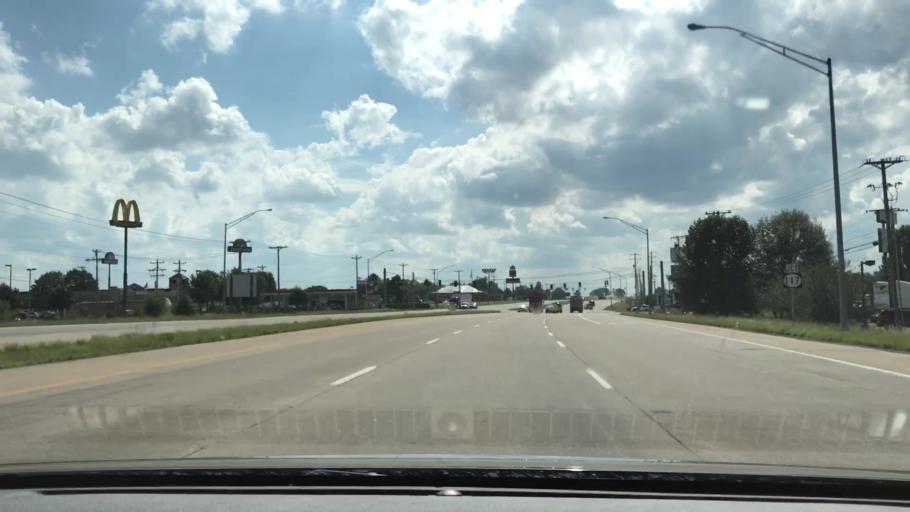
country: US
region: Kentucky
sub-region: Christian County
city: Oak Grove
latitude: 36.6980
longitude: -87.4537
